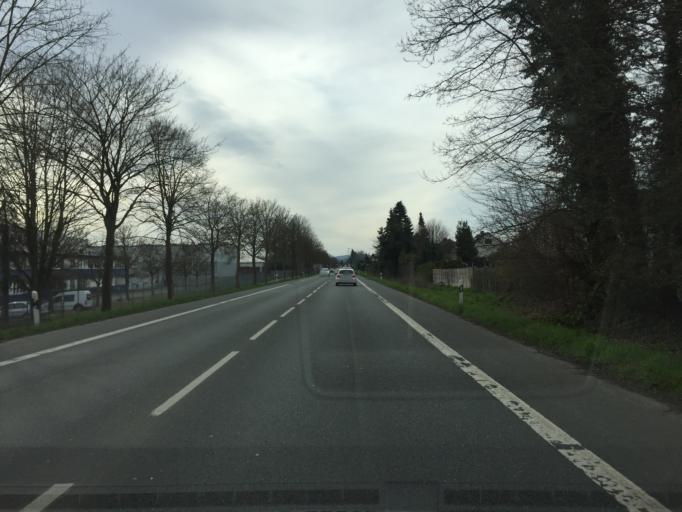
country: DE
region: North Rhine-Westphalia
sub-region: Regierungsbezirk Detmold
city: Bad Salzuflen
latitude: 52.0462
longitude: 8.7586
